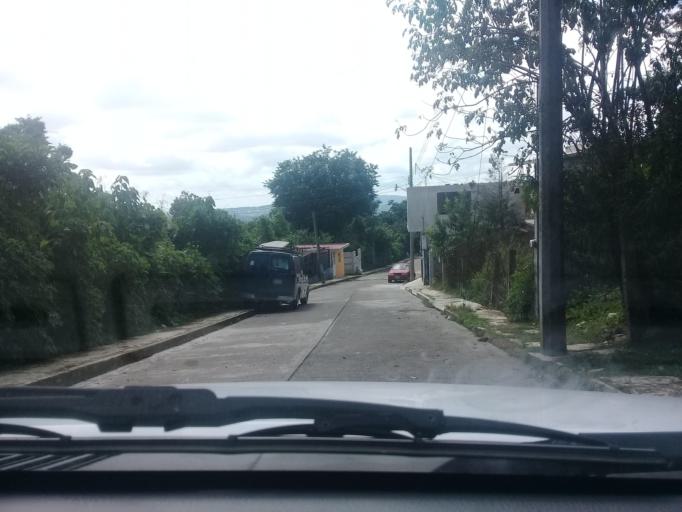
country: MX
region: Veracruz
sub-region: Tlalnelhuayocan
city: Otilpan
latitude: 19.5607
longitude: -96.9795
